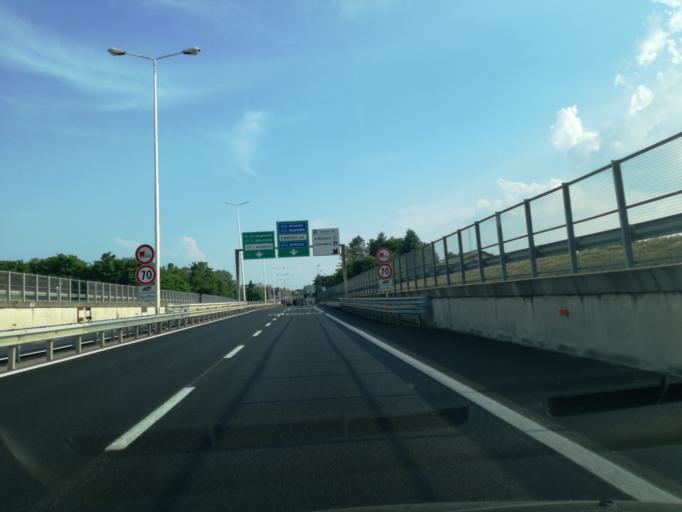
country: IT
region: Lombardy
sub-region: Provincia di Monza e Brianza
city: Velasca
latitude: 45.6237
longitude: 9.3609
